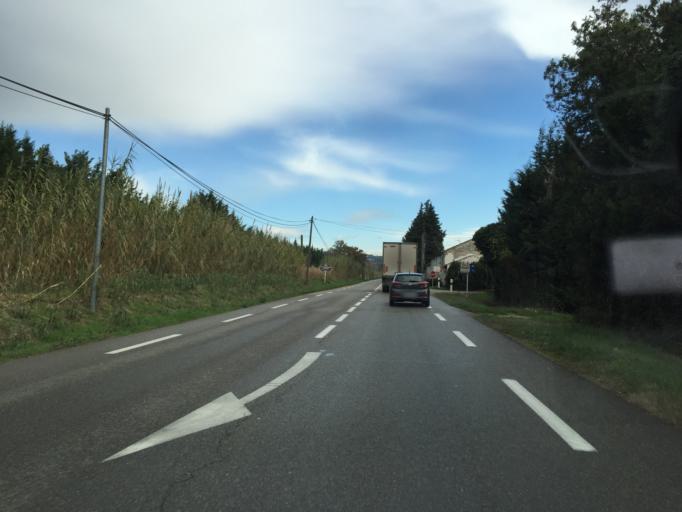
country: FR
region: Provence-Alpes-Cote d'Azur
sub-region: Departement du Vaucluse
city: Lagnes
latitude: 43.8749
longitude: 5.0893
